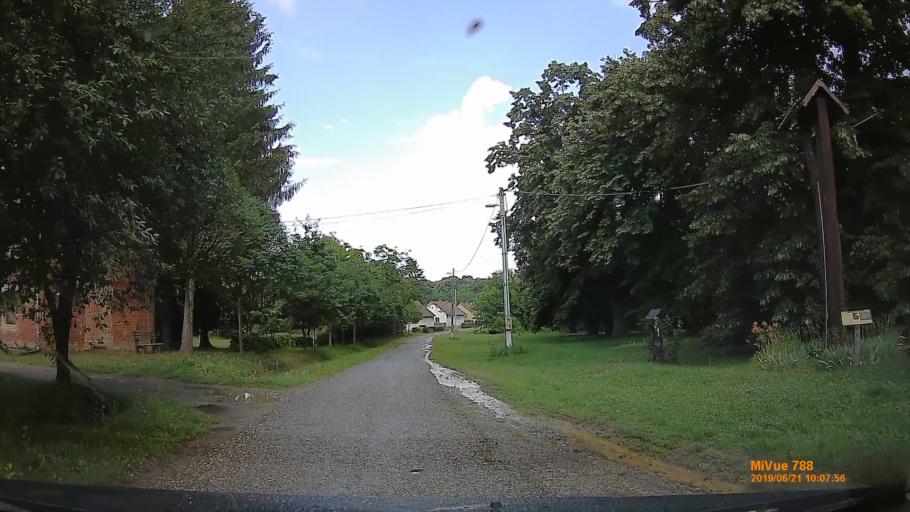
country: HU
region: Baranya
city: Buekkoesd
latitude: 46.1921
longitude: 17.9590
